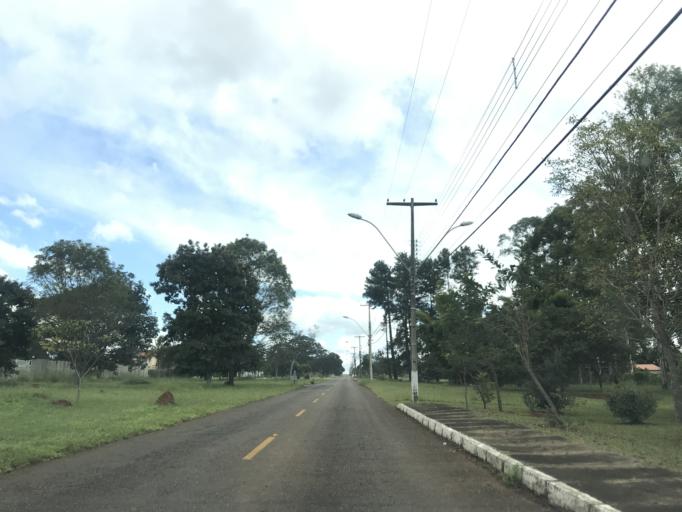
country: BR
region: Federal District
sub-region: Brasilia
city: Brasilia
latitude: -15.8918
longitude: -47.9251
